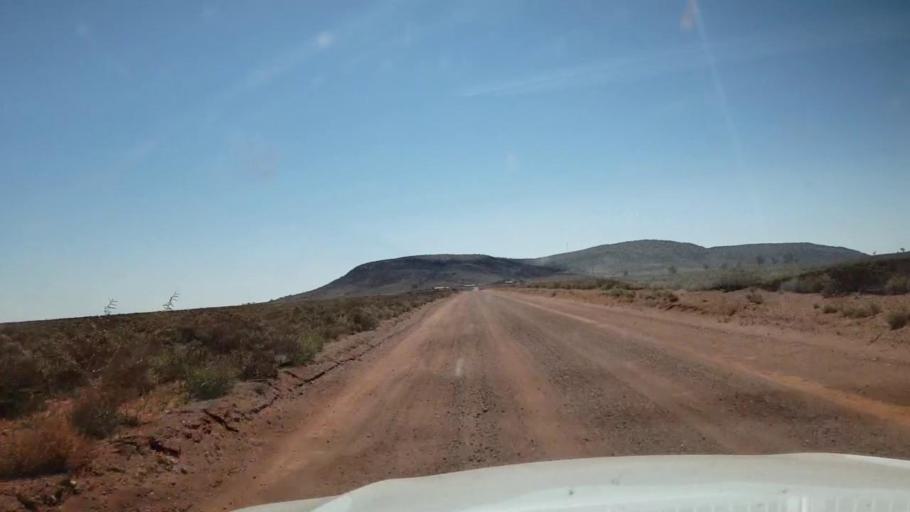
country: AU
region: South Australia
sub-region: Whyalla
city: Whyalla
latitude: -32.7002
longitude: 137.1341
